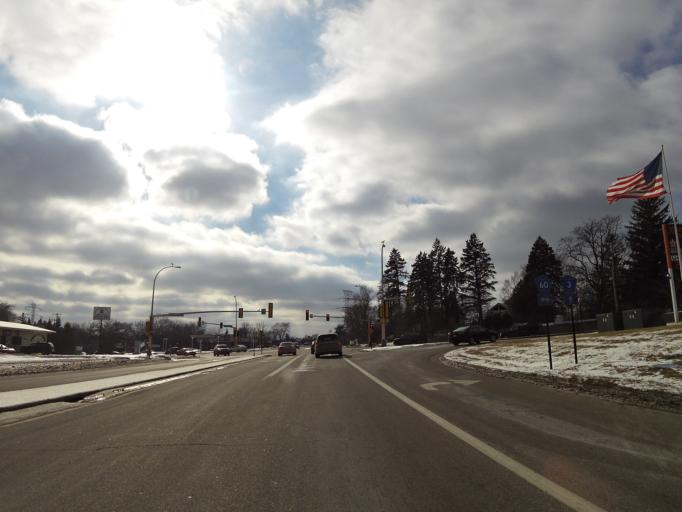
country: US
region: Minnesota
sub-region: Hennepin County
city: Hopkins
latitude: 44.9164
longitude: -93.4469
